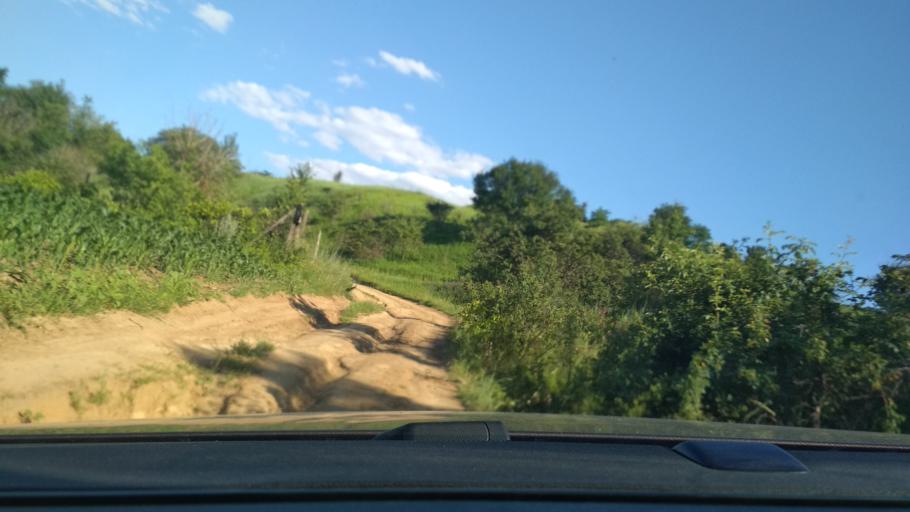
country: MD
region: Stinga Nistrului
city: Bucovat
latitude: 47.1333
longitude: 28.4282
